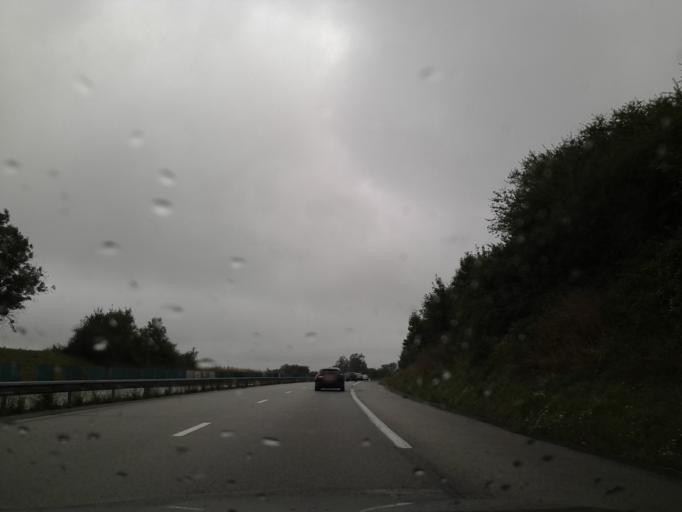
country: FR
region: Lower Normandy
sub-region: Departement de la Manche
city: Sainte-Mere-Eglise
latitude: 49.3954
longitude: -1.3068
